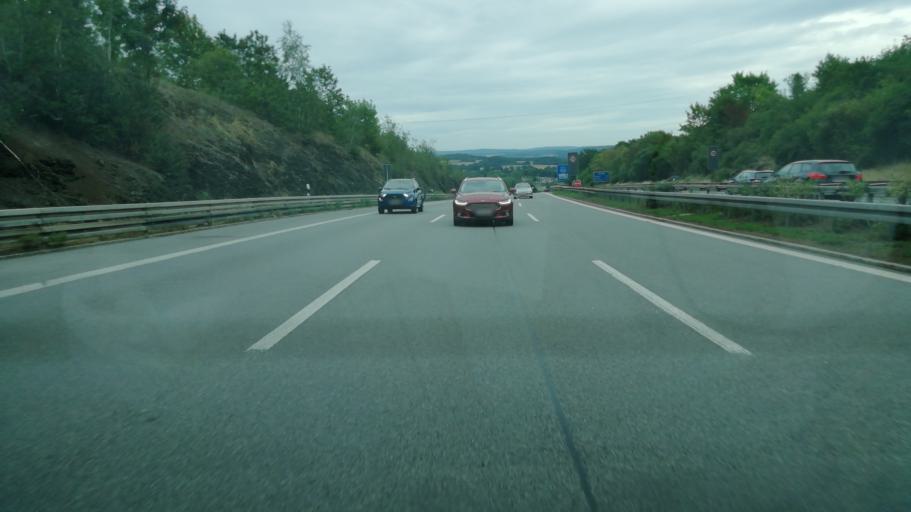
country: DE
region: Saxony
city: Weischlitz
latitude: 50.4351
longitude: 12.0964
